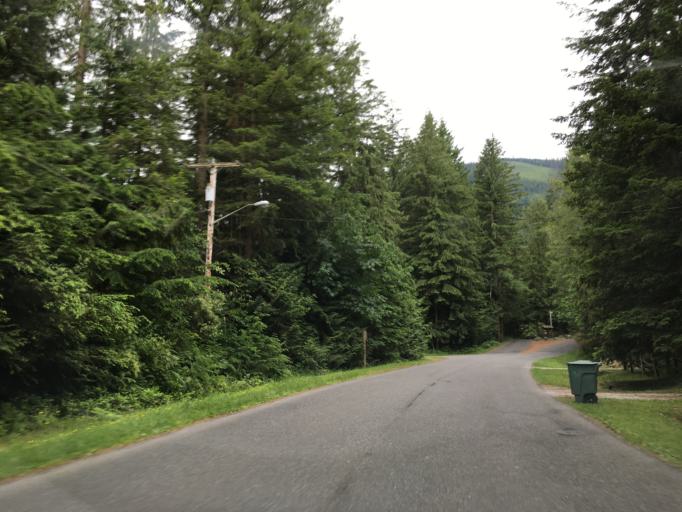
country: US
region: Washington
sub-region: Whatcom County
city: Peaceful Valley
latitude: 48.9388
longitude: -122.1452
